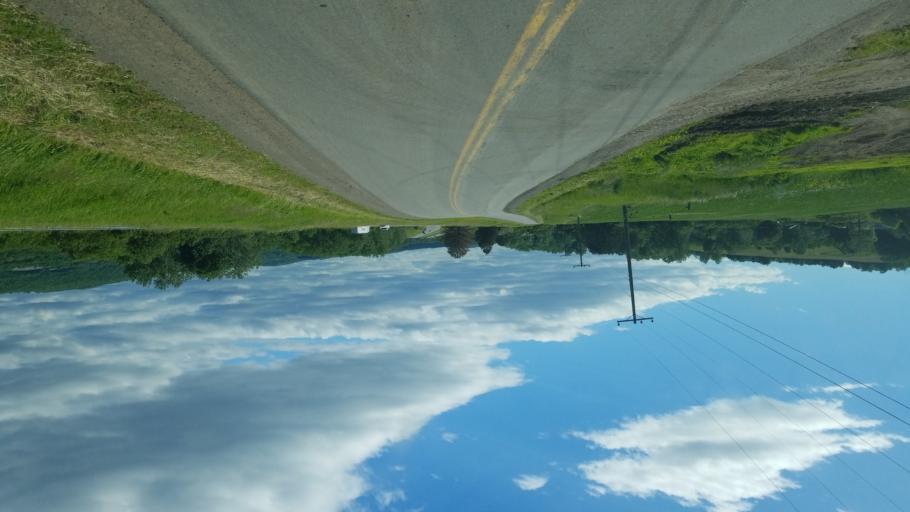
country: US
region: New York
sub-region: Montgomery County
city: Fort Plain
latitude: 42.9622
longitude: -74.6403
